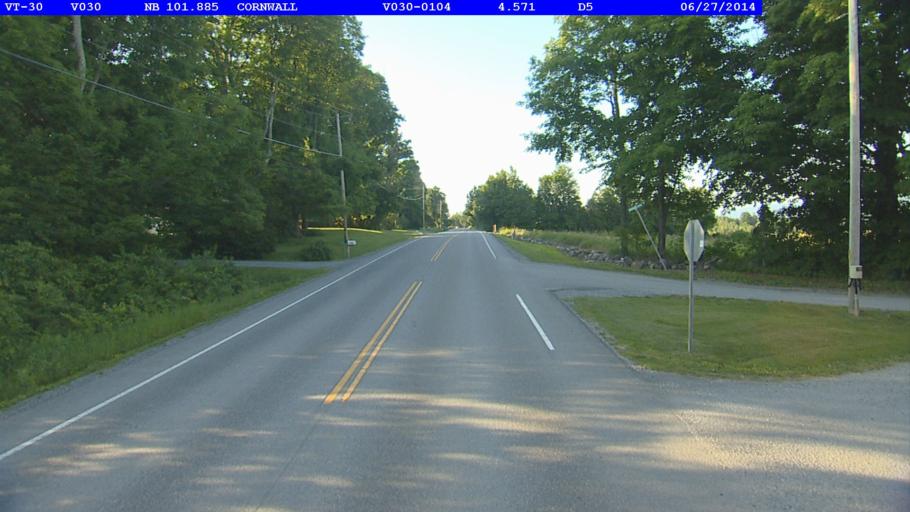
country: US
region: Vermont
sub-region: Addison County
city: Middlebury (village)
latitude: 43.9732
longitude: -73.2060
